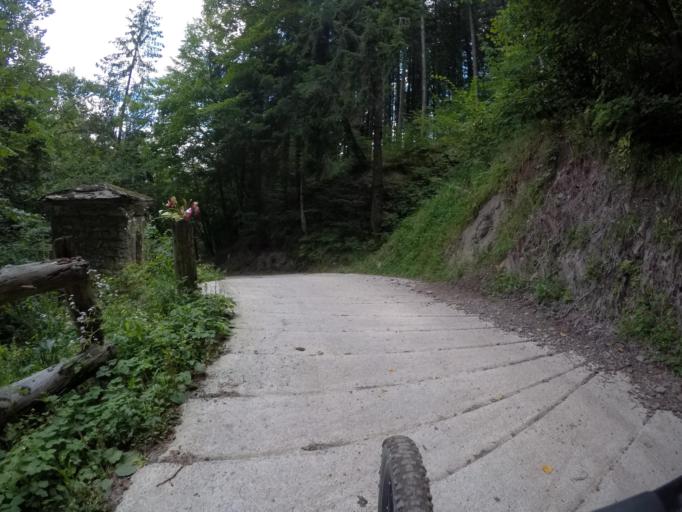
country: IT
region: Friuli Venezia Giulia
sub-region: Provincia di Udine
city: Arta Terme
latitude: 46.4790
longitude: 13.0608
